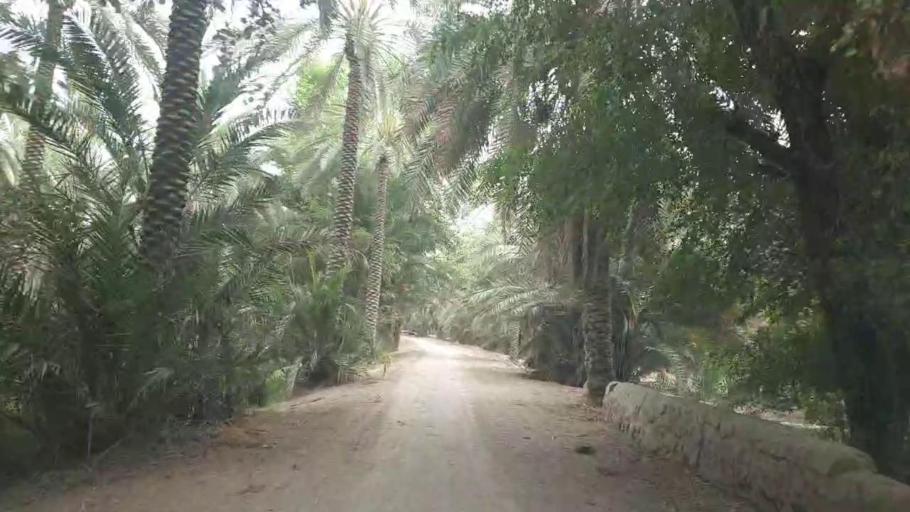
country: PK
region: Sindh
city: Khairpur
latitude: 27.5817
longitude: 68.7489
